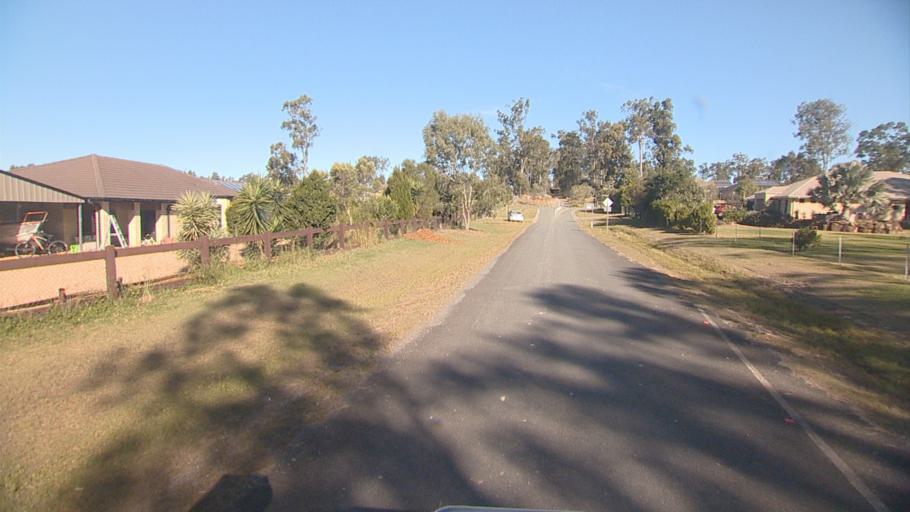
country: AU
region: Queensland
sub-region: Ipswich
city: Springfield Lakes
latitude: -27.7403
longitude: 152.9216
